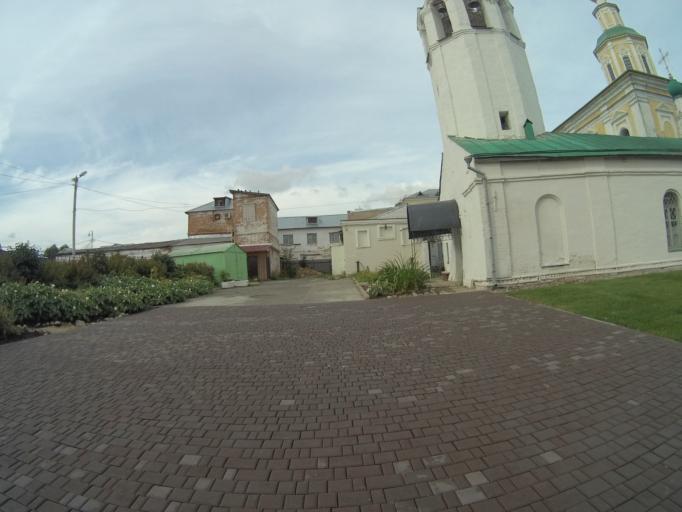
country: RU
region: Vladimir
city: Vladimir
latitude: 56.1267
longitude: 40.4020
